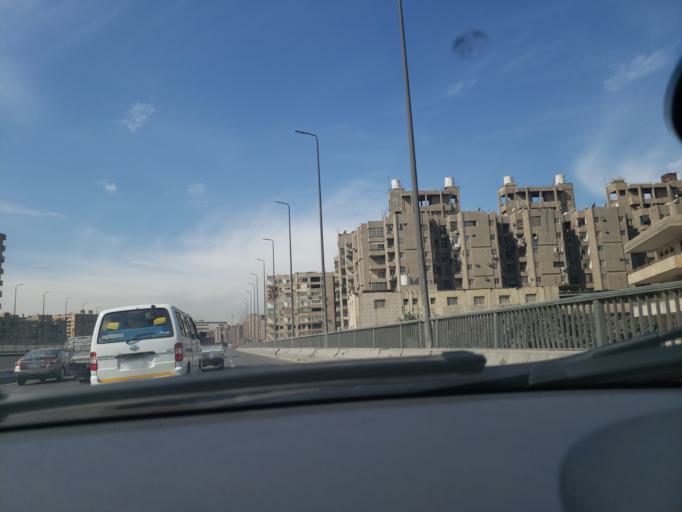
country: EG
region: Al Jizah
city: Al Jizah
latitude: 29.9782
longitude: 31.1624
